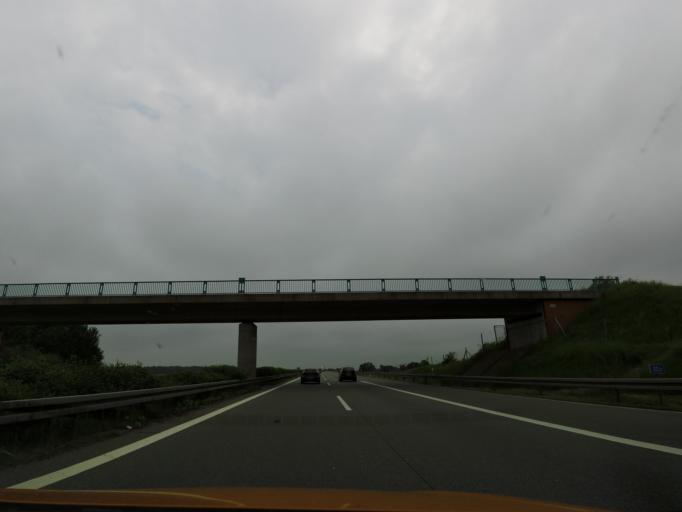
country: DE
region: Mecklenburg-Vorpommern
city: Selmsdorf
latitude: 53.8155
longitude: 10.8836
